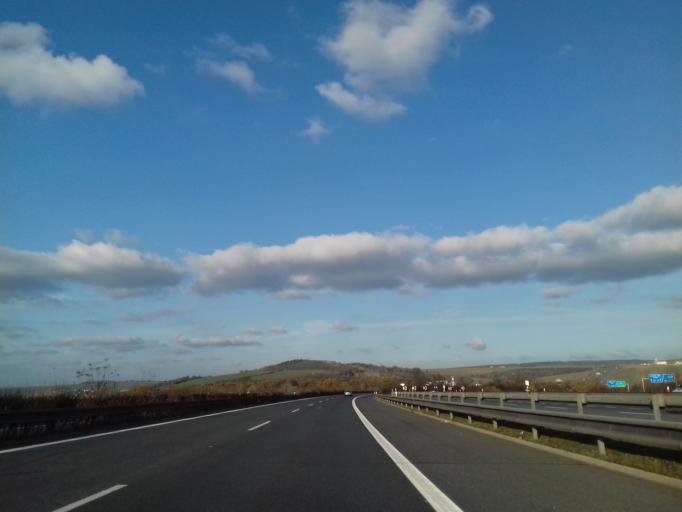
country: CZ
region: Plzensky
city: Stary Plzenec
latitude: 49.7004
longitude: 13.4320
